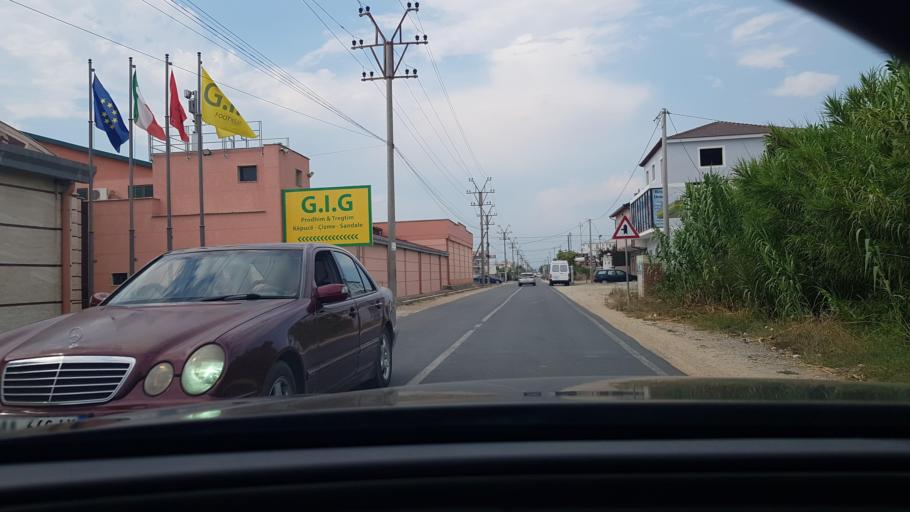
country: AL
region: Durres
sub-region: Rrethi i Durresit
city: Sukth
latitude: 41.3956
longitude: 19.5465
